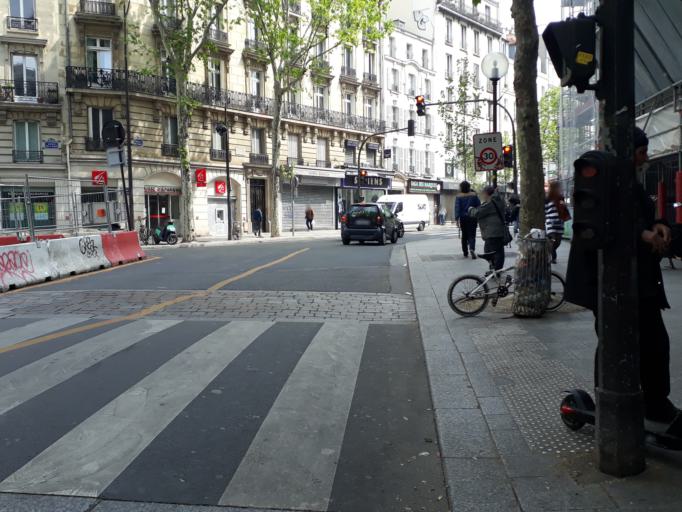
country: FR
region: Ile-de-France
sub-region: Paris
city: Saint-Ouen
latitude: 48.8876
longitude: 2.3254
